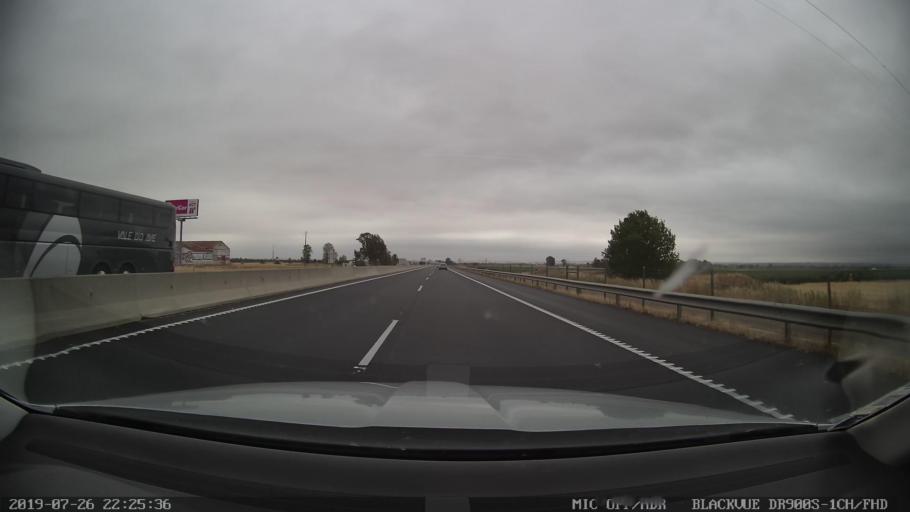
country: PT
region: Portalegre
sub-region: Elvas
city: Elvas
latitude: 38.8853
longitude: -7.0716
